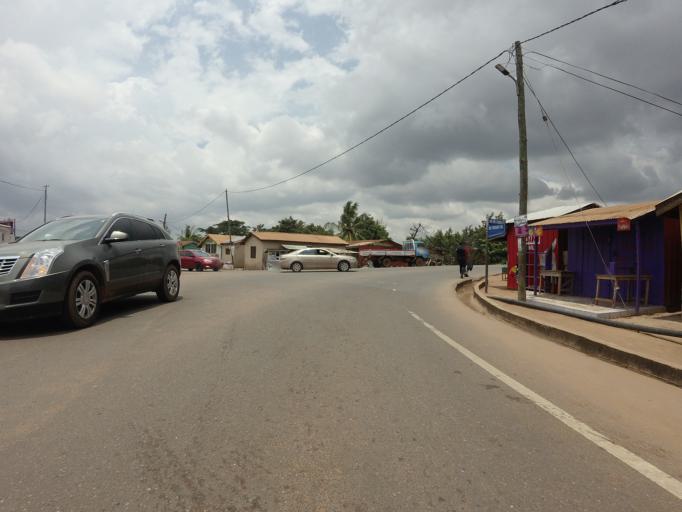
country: GH
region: Greater Accra
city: Medina Estates
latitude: 5.6797
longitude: -0.1508
